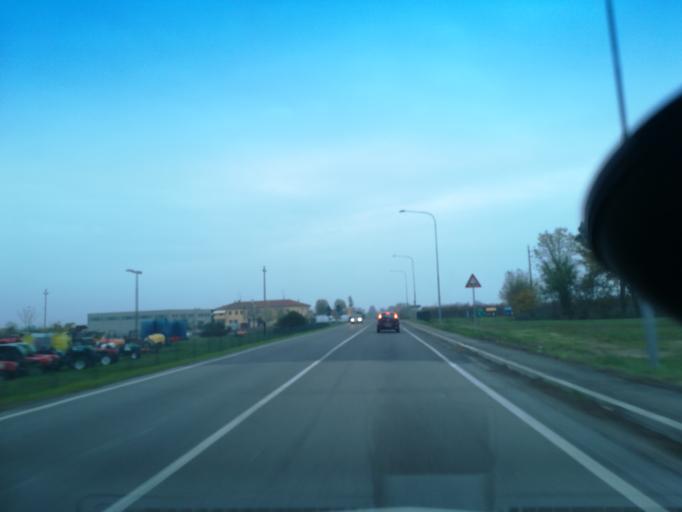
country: IT
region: Emilia-Romagna
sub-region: Provincia di Ravenna
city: Castel Bolognese
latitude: 44.3356
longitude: 11.7595
